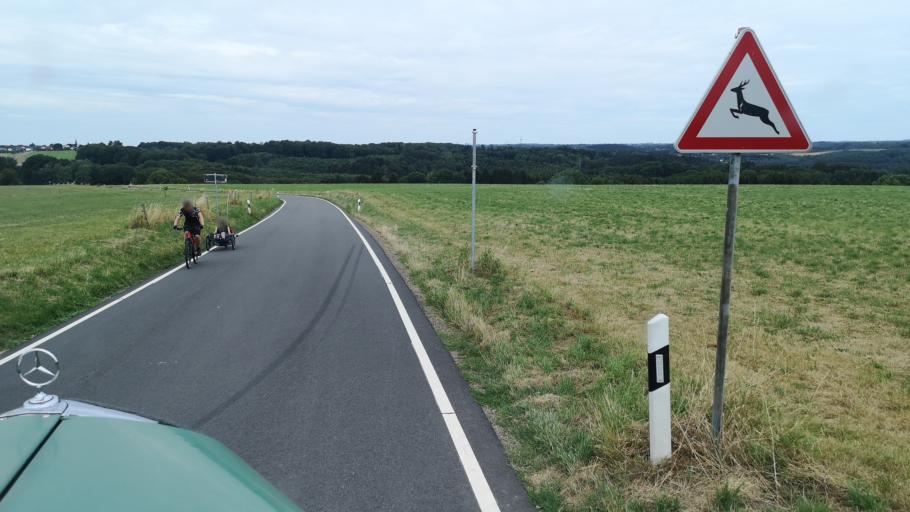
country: DE
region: North Rhine-Westphalia
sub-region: Regierungsbezirk Koln
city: Kurten
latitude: 51.0479
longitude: 7.2001
